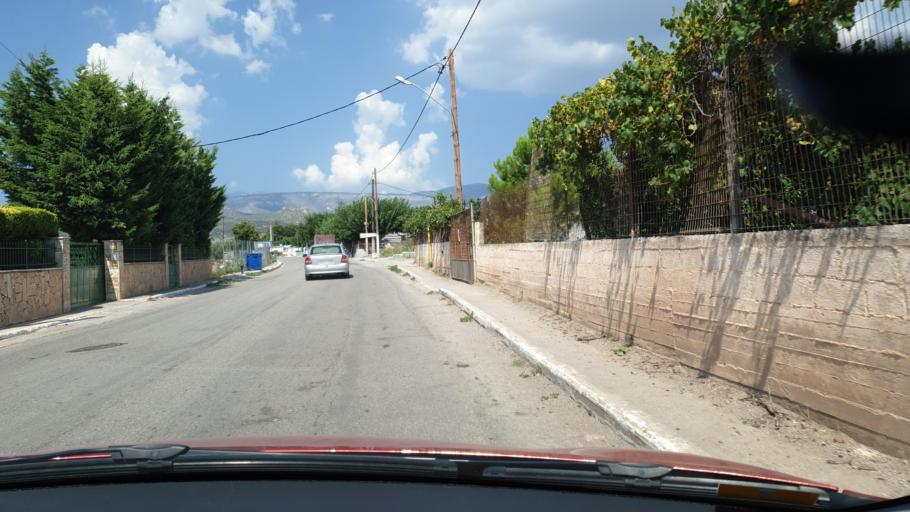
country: GR
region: Central Greece
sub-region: Nomos Evvoias
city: Kastella
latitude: 38.5726
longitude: 23.6320
